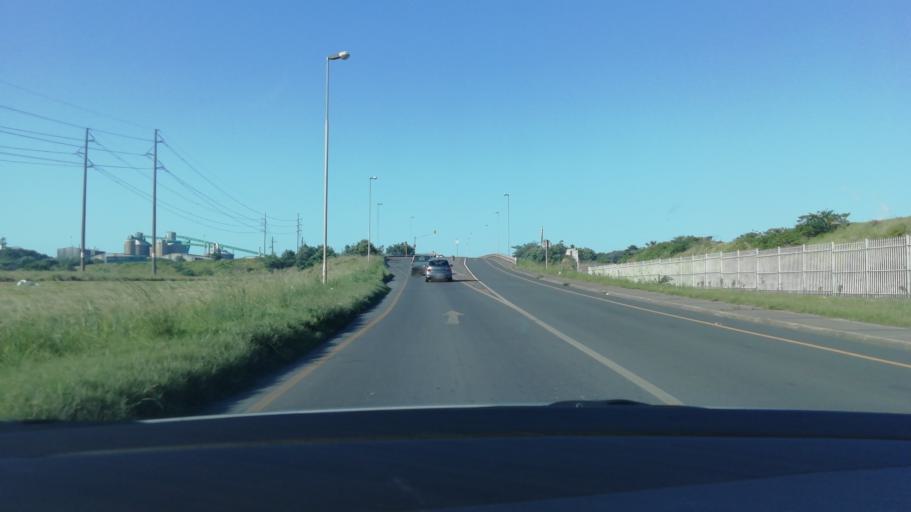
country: ZA
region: KwaZulu-Natal
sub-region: uThungulu District Municipality
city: Richards Bay
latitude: -28.7729
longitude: 32.0330
